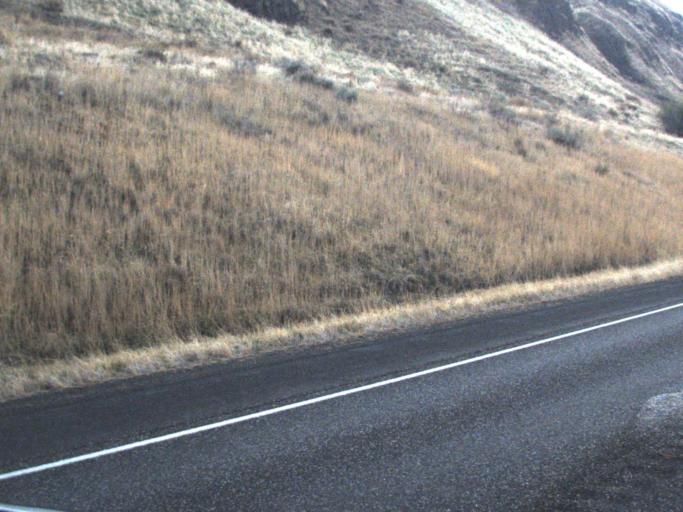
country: US
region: Washington
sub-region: Asotin County
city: Clarkston Heights-Vineland
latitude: 46.4250
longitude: -117.1606
